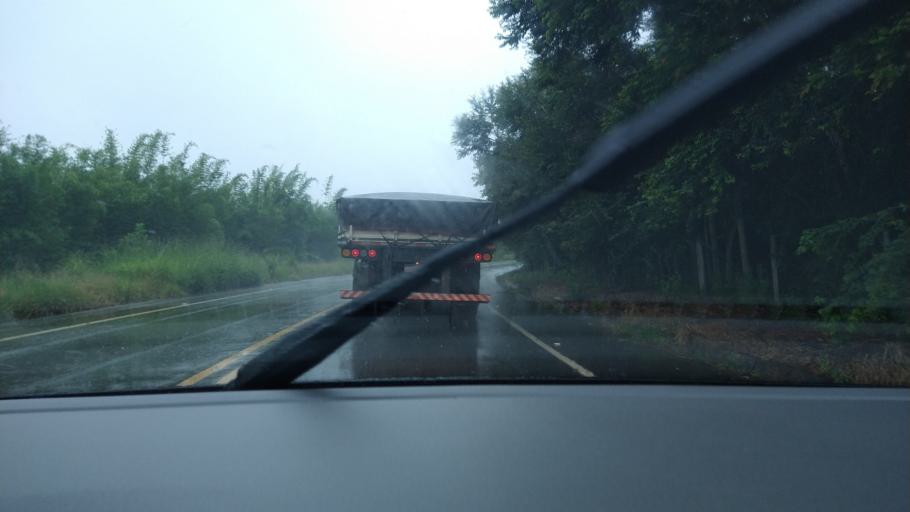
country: BR
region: Minas Gerais
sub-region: Ponte Nova
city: Ponte Nova
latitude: -20.5738
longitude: -42.8752
